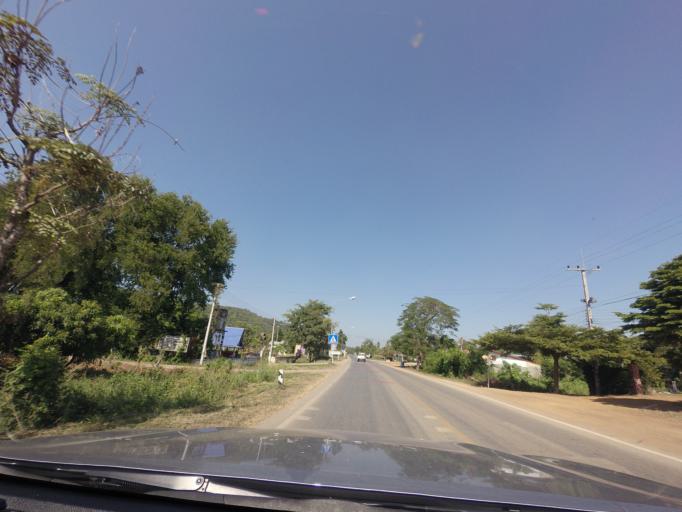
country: TH
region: Sukhothai
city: Sawankhalok
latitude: 17.3938
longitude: 99.7954
